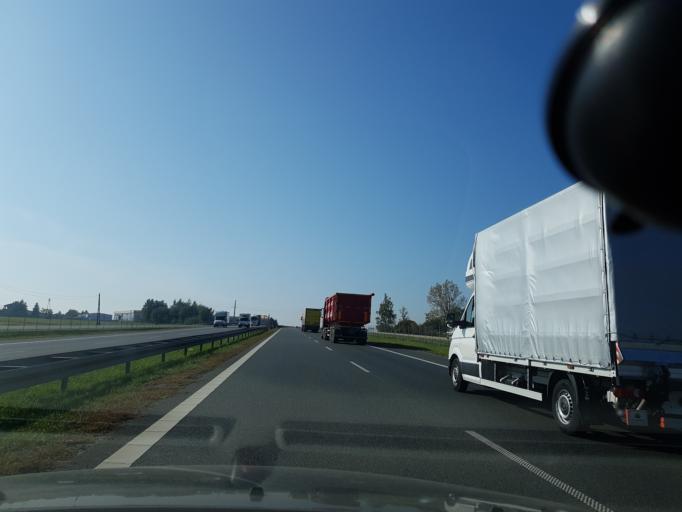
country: PL
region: Masovian Voivodeship
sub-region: Powiat zyrardowski
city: Radziejowice
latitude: 51.9884
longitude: 20.5391
